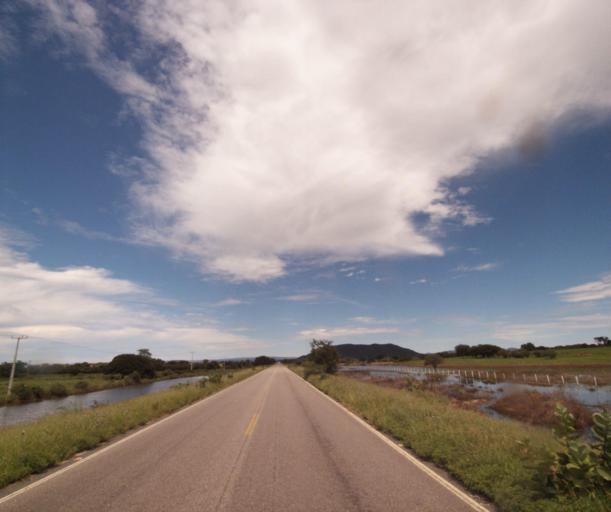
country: BR
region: Bahia
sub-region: Guanambi
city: Guanambi
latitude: -14.2288
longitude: -42.9209
